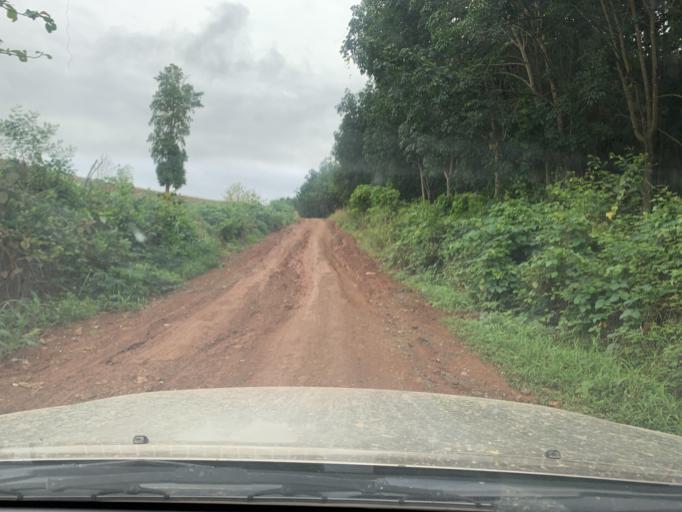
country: TH
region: Nan
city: Mae Charim
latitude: 18.4110
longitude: 101.4410
